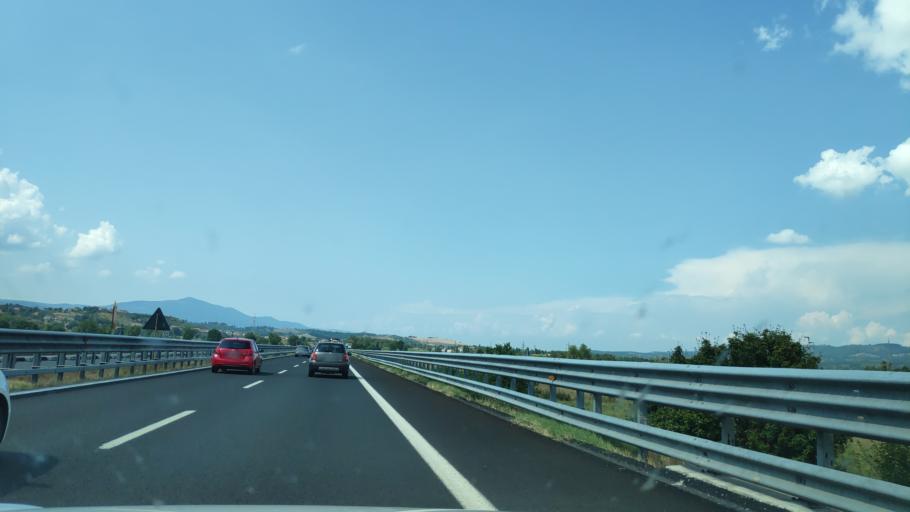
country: IT
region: Umbria
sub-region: Provincia di Terni
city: Fabro Scalo
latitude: 42.8631
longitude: 12.0347
